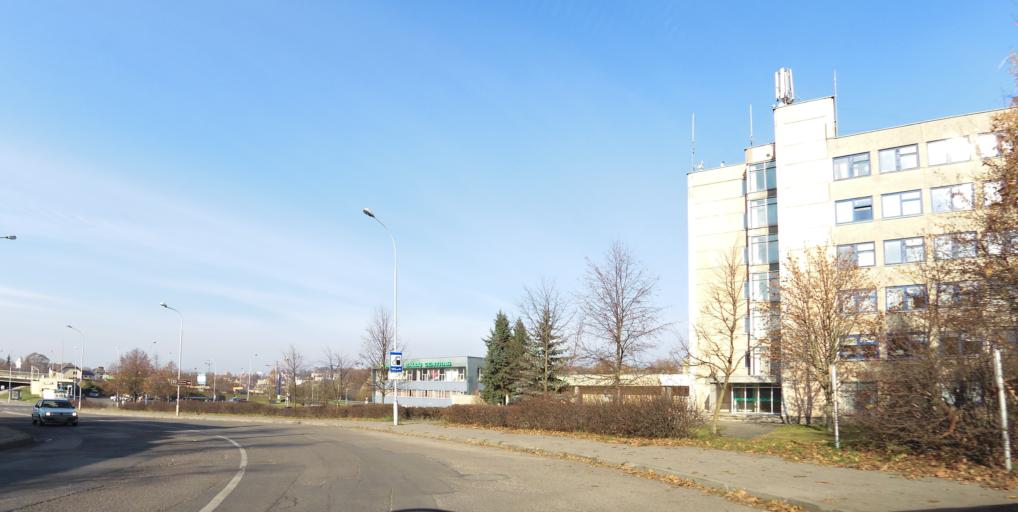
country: LT
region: Vilnius County
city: Rasos
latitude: 54.6760
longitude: 25.3115
